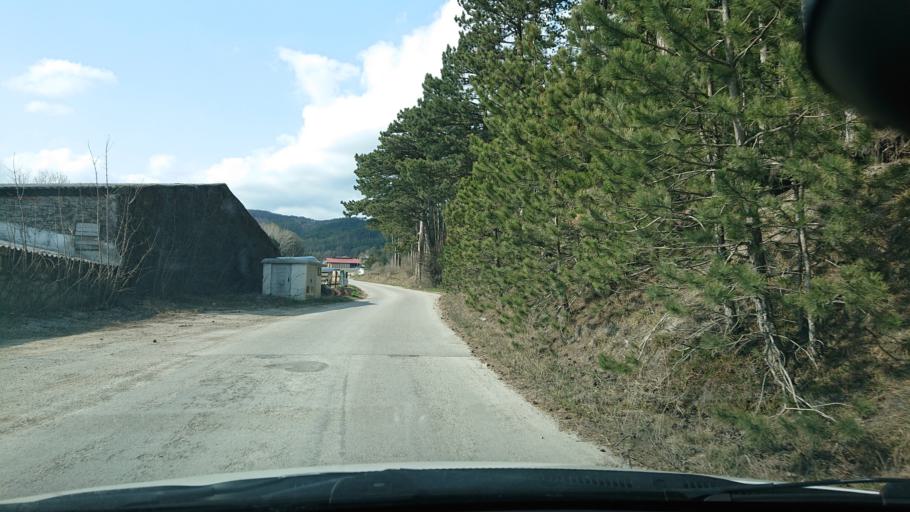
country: AT
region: Lower Austria
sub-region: Politischer Bezirk Baden
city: Pottenstein
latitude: 47.9399
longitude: 16.0728
